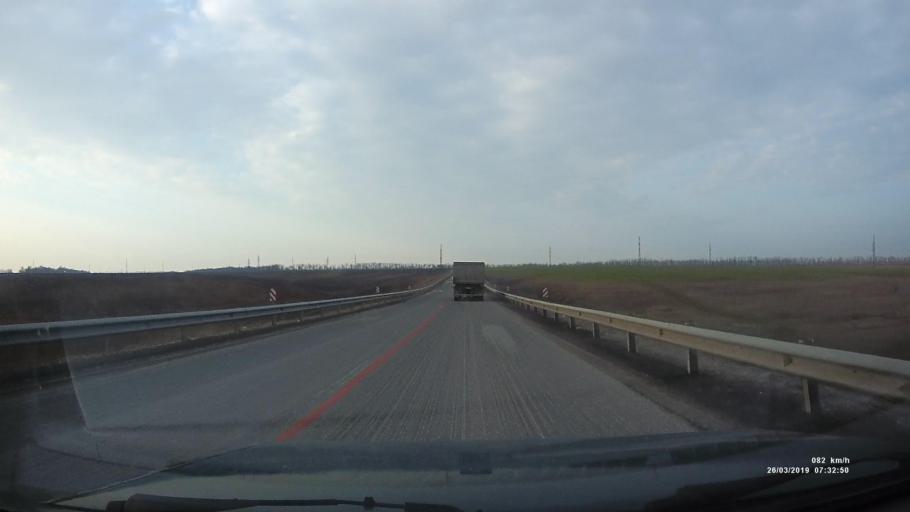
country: RU
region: Rostov
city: Novobessergenovka
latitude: 47.2208
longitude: 38.7743
